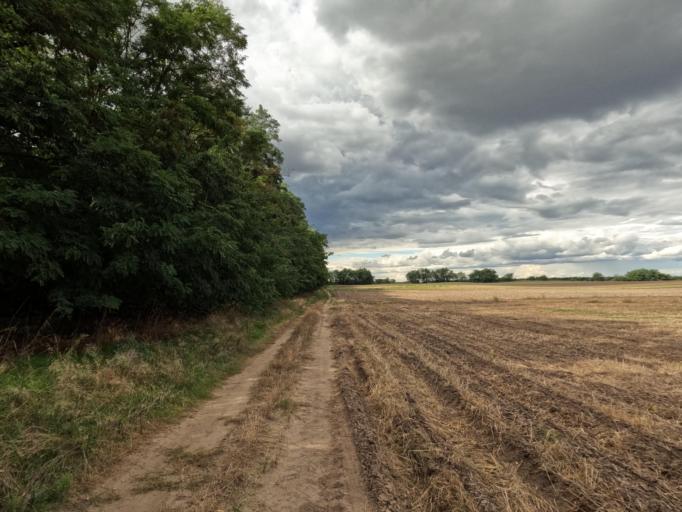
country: HU
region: Tolna
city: Tengelic
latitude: 46.5202
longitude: 18.6771
